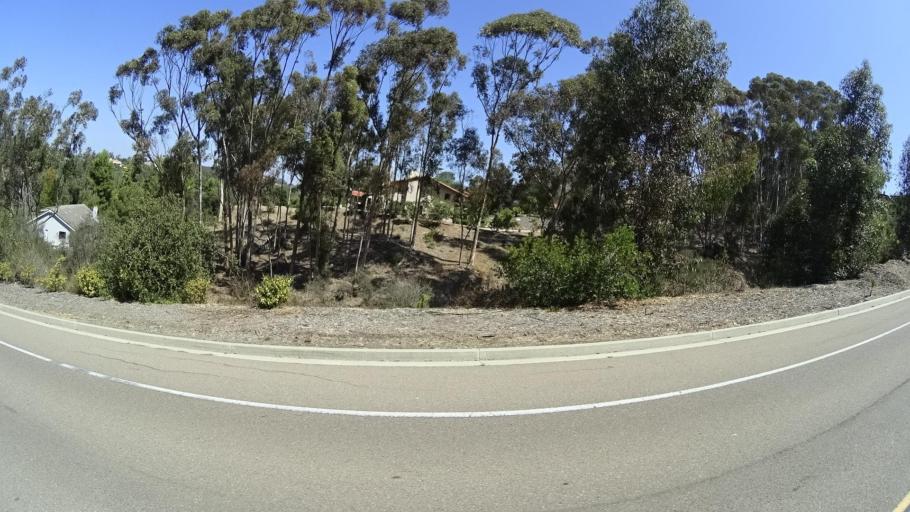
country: US
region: California
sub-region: San Diego County
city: Fairbanks Ranch
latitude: 32.9755
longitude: -117.1792
